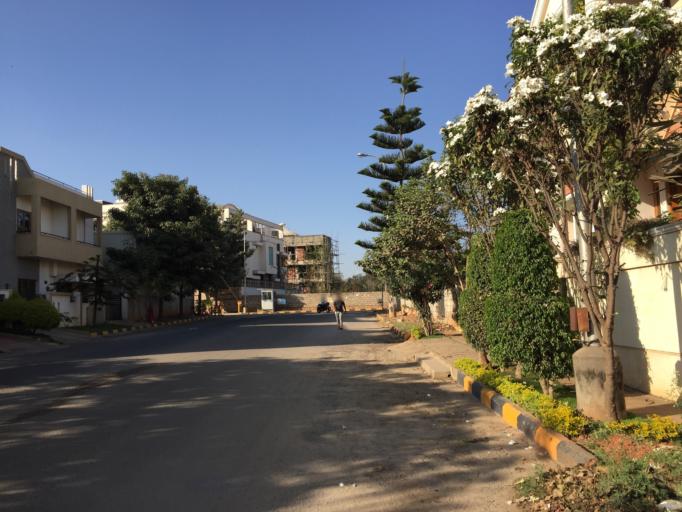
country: IN
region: Karnataka
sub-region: Bangalore Urban
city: Yelahanka
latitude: 13.0546
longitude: 77.6252
